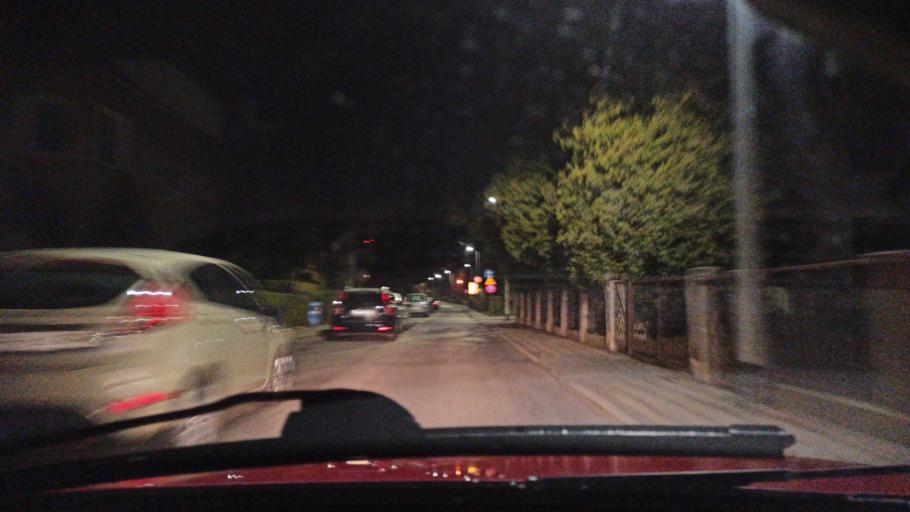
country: PL
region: Warmian-Masurian Voivodeship
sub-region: Powiat elblaski
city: Elblag
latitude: 54.1684
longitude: 19.4139
